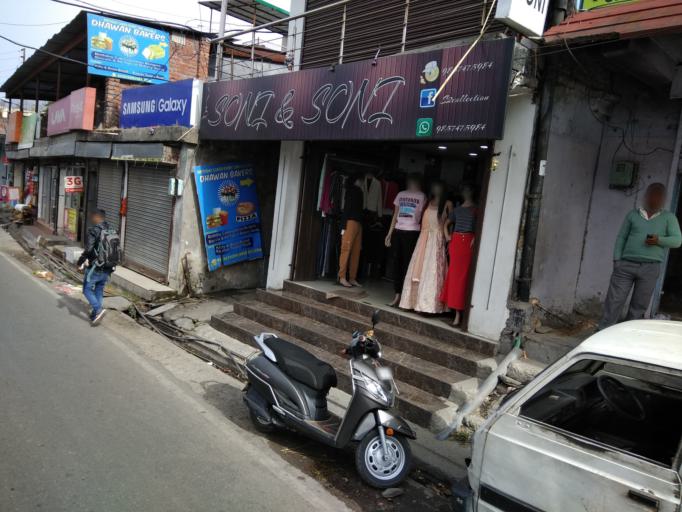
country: IN
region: Himachal Pradesh
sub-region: Kangra
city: Dharmsala
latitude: 32.1830
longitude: 76.3746
